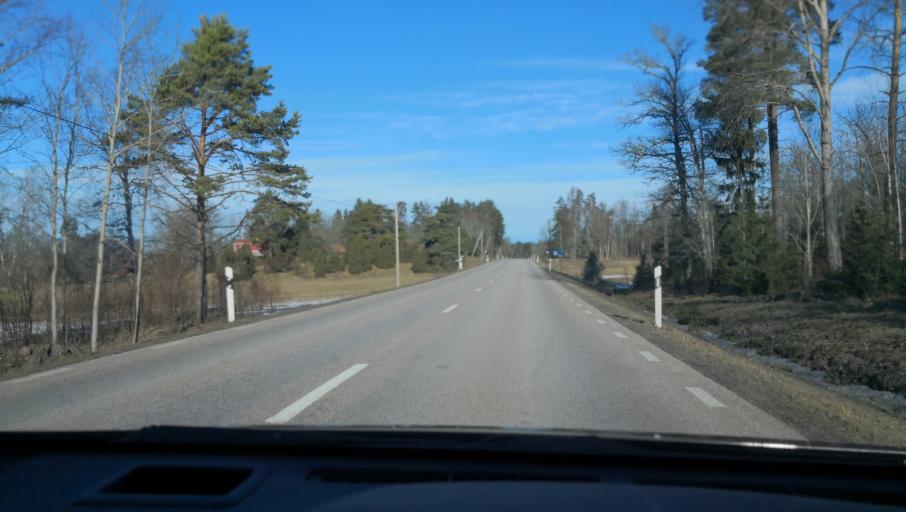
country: SE
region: Uppsala
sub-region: Osthammars Kommun
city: Osterbybruk
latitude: 60.1642
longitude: 17.8420
